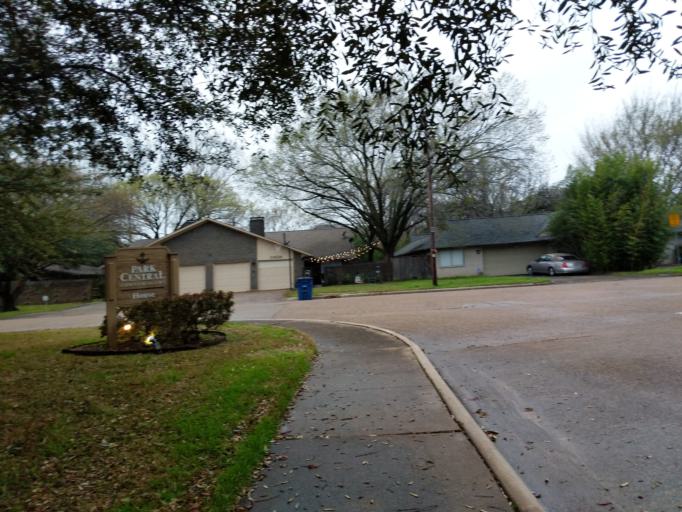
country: US
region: Texas
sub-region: Dallas County
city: Richardson
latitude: 32.9040
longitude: -96.7711
